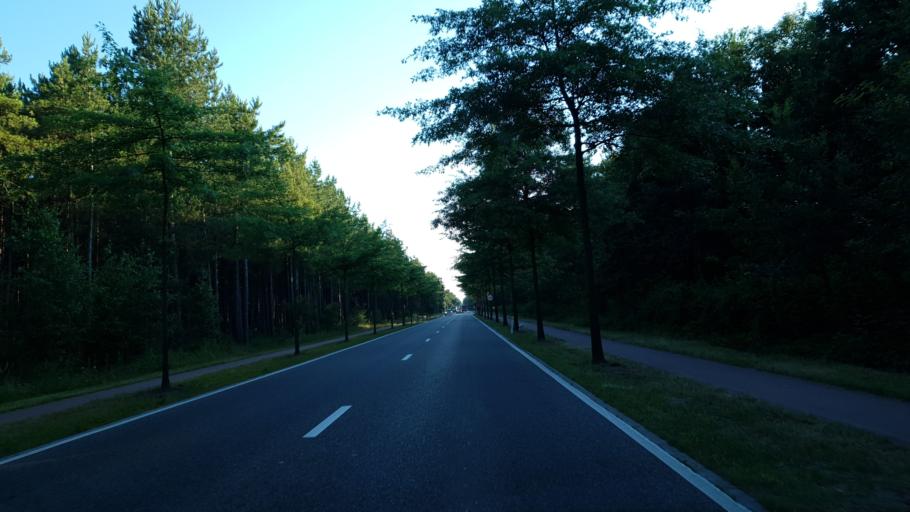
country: BE
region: Flanders
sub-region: Provincie Antwerpen
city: Beerse
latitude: 51.2940
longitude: 4.8555
